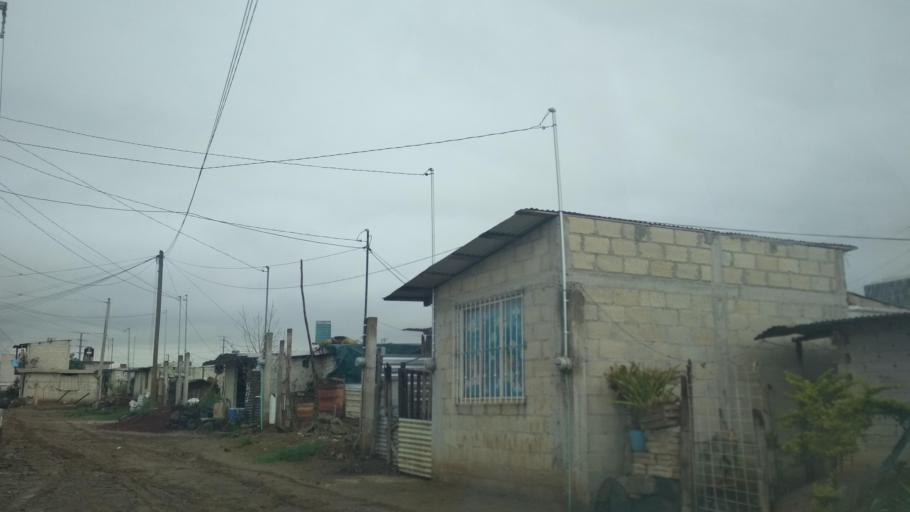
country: MX
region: Veracruz
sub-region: Emiliano Zapata
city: Las Trancas
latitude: 19.5065
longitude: -96.8712
